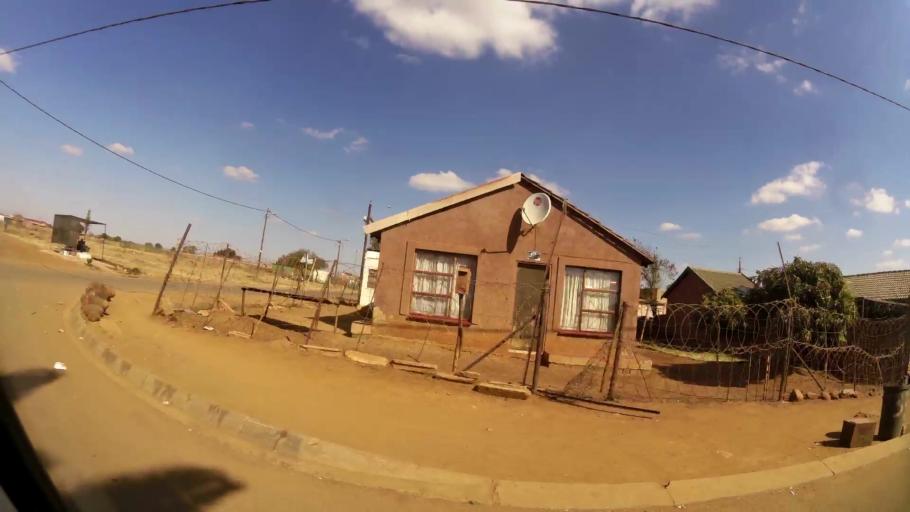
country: ZA
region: Gauteng
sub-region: City of Tshwane Metropolitan Municipality
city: Cullinan
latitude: -25.7184
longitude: 28.4042
